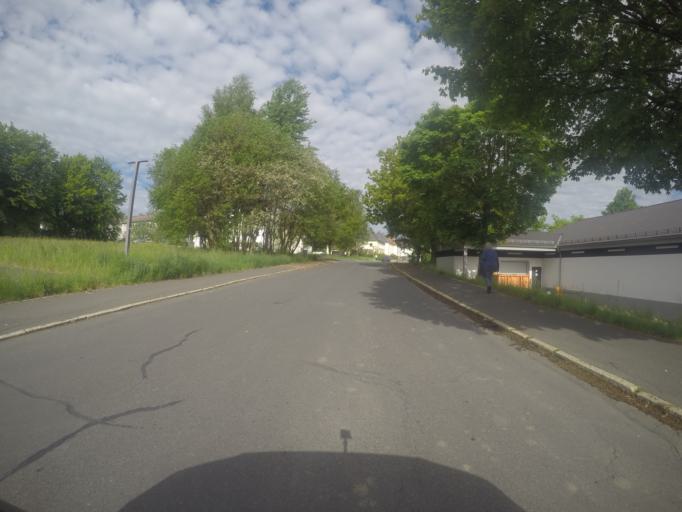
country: DE
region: Bavaria
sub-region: Upper Franconia
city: Schonwald
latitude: 50.1971
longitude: 12.0919
